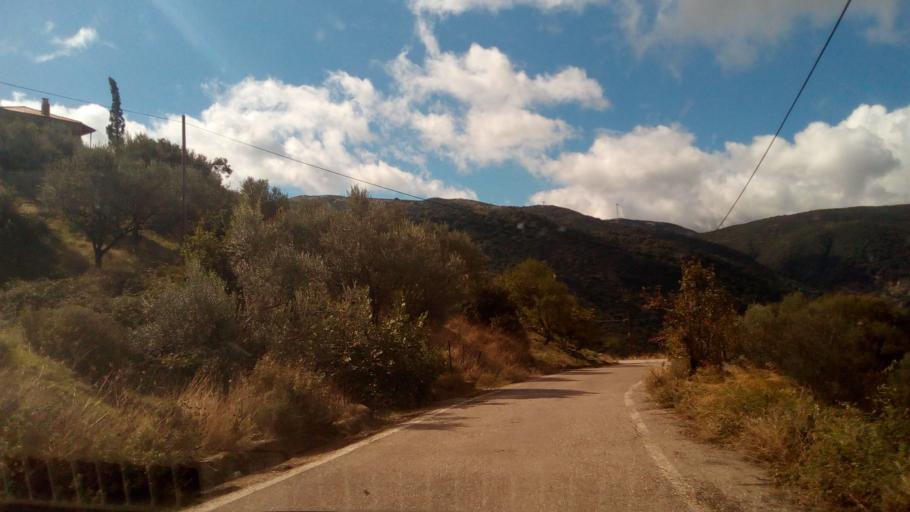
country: GR
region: West Greece
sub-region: Nomos Aitolias kai Akarnanias
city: Nafpaktos
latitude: 38.4874
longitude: 21.8522
